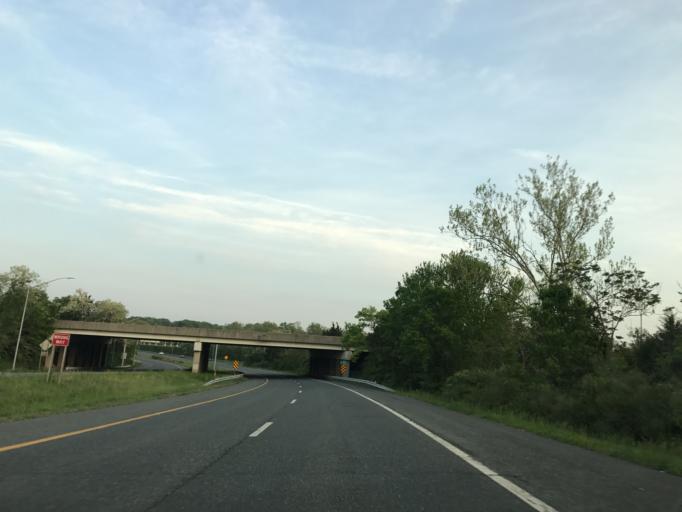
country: US
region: Maryland
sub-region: Anne Arundel County
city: Pumphrey
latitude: 39.2057
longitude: -76.6241
